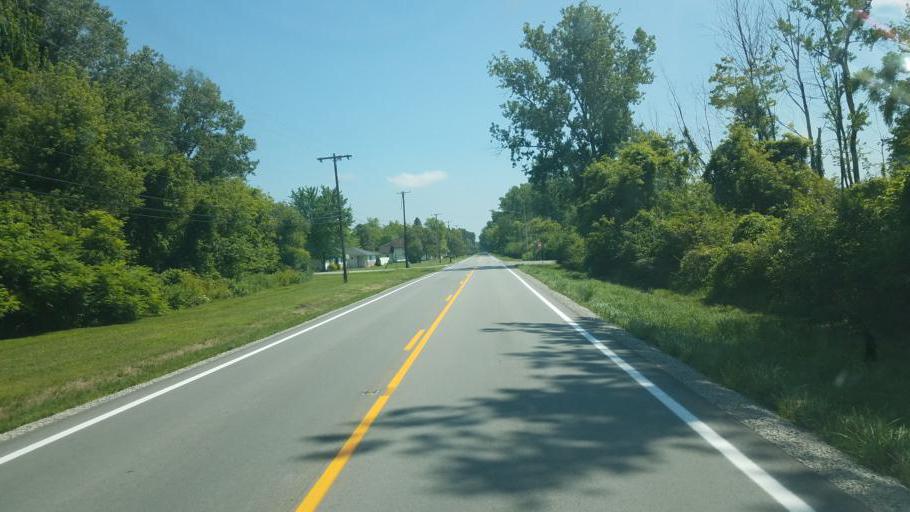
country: US
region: Ohio
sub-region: Erie County
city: Sandusky
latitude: 41.4179
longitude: -82.8168
